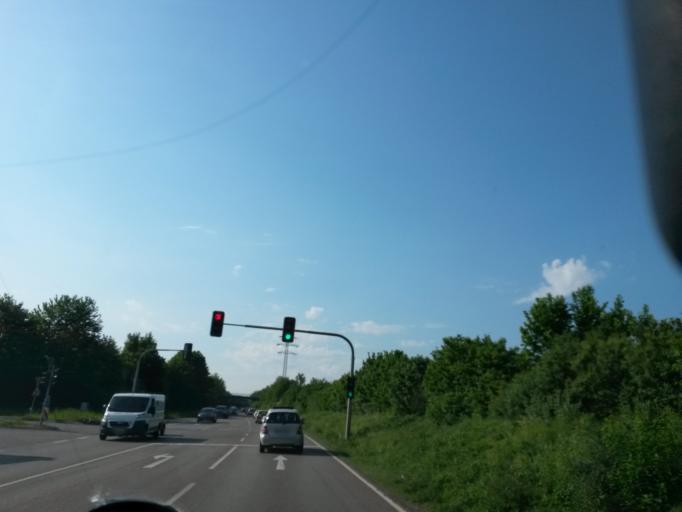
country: DE
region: Baden-Wuerttemberg
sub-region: Regierungsbezirk Stuttgart
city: Denkendorf
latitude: 48.7137
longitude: 9.3091
